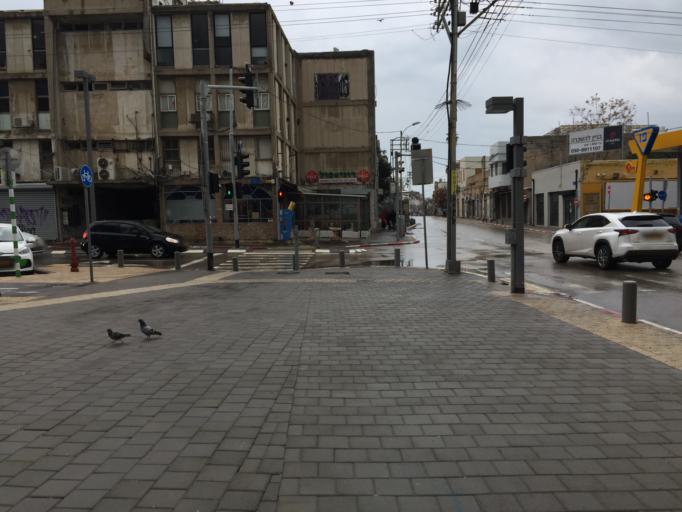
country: IL
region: Tel Aviv
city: Yafo
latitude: 32.0580
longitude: 34.7643
